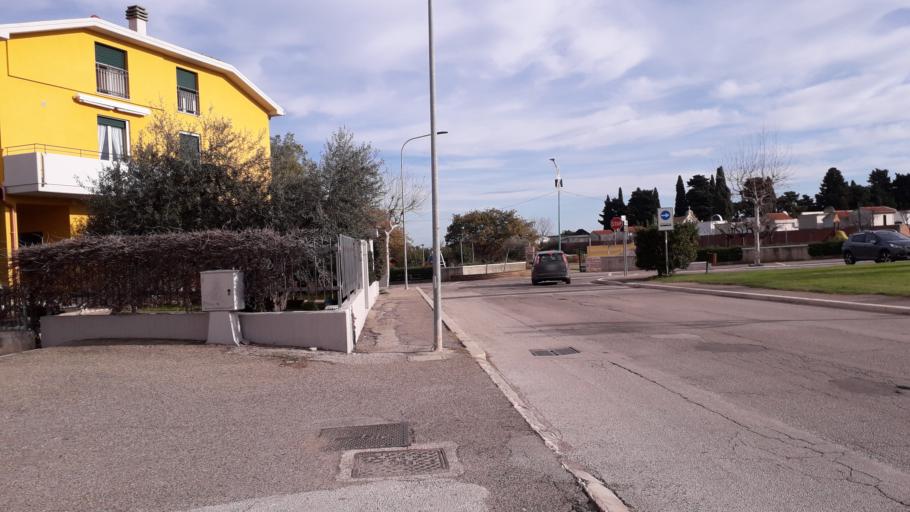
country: IT
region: Molise
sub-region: Provincia di Campobasso
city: Campomarino
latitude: 41.9526
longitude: 15.0355
